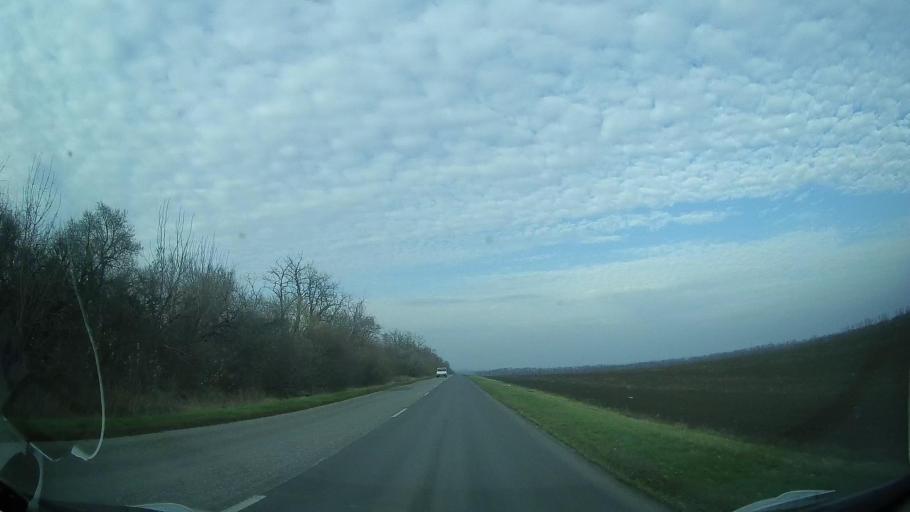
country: RU
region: Rostov
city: Bagayevskaya
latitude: 47.0818
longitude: 40.3915
